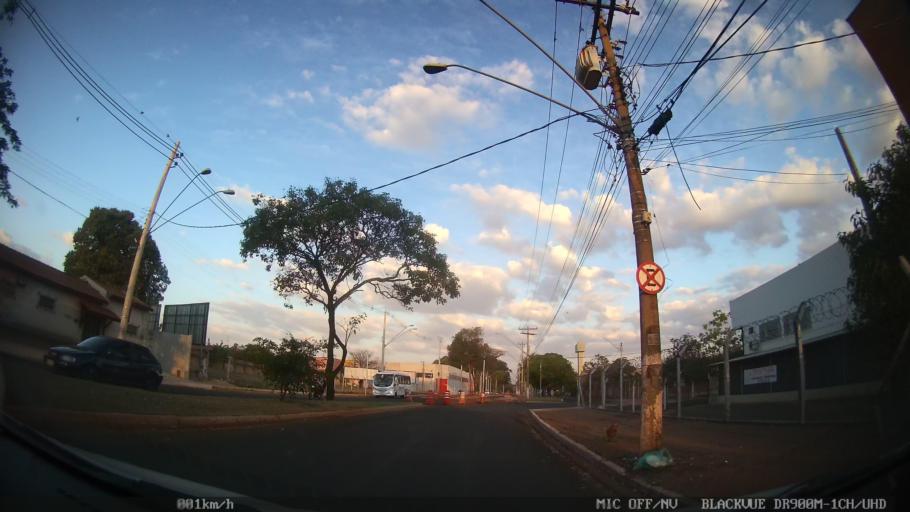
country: BR
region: Sao Paulo
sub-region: Ribeirao Preto
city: Ribeirao Preto
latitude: -21.1480
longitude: -47.7869
